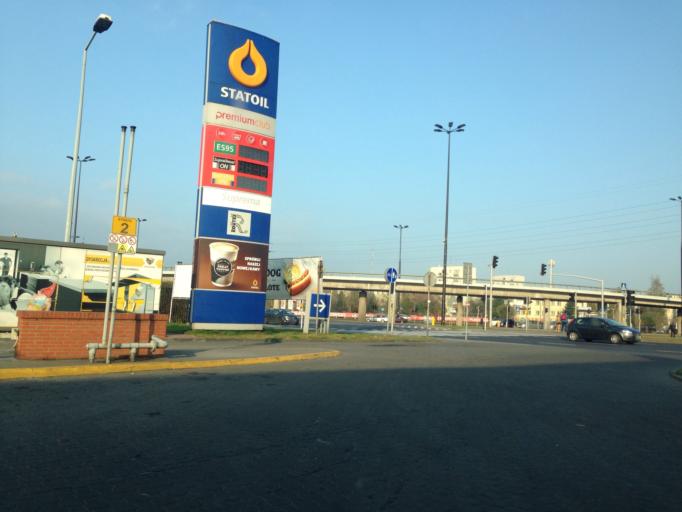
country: PL
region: Masovian Voivodeship
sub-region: Warszawa
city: Ursynow
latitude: 52.1523
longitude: 21.0171
